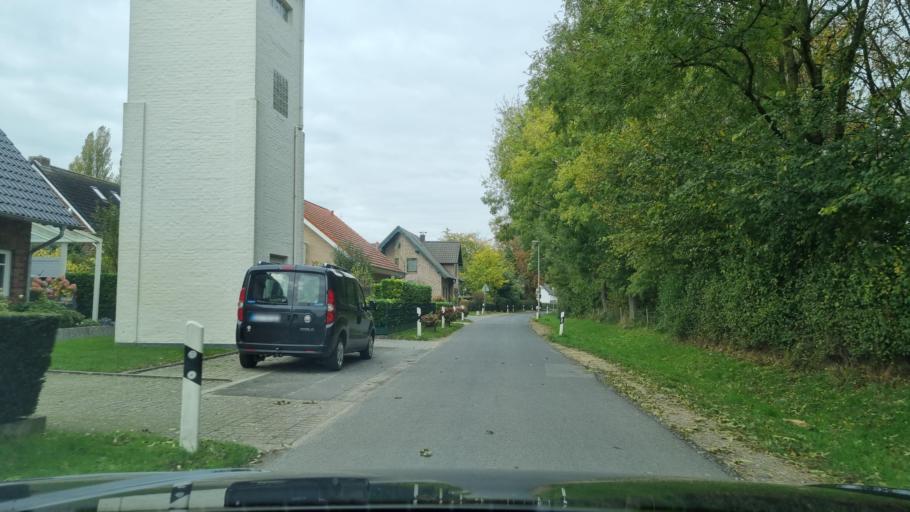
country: DE
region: North Rhine-Westphalia
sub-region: Regierungsbezirk Dusseldorf
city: Kleve
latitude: 51.8293
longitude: 6.1100
